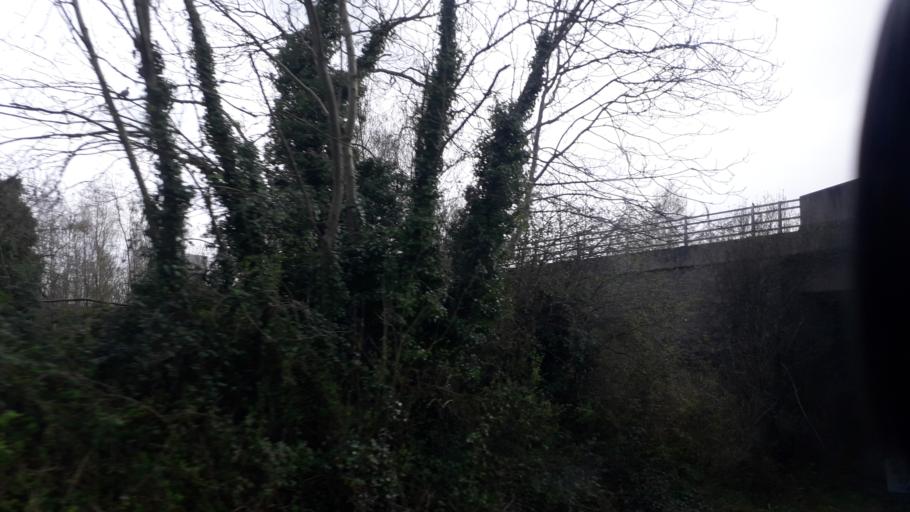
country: IE
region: Leinster
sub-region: An Mhi
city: Enfield
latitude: 53.4133
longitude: -6.8403
